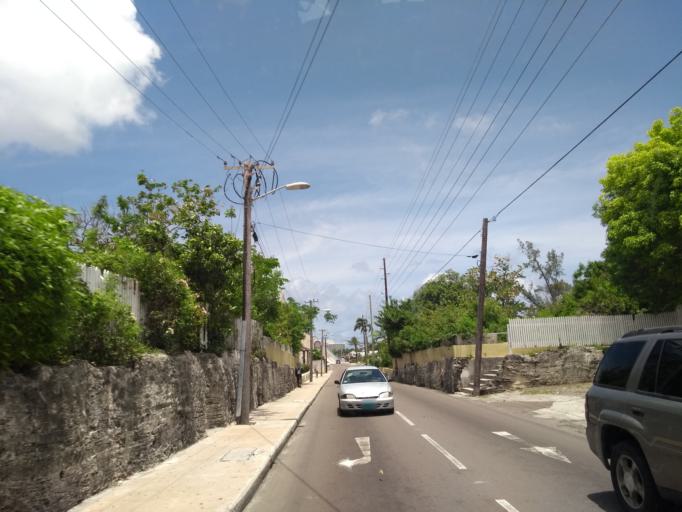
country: BS
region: New Providence
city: Nassau
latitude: 25.0733
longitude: -77.3227
